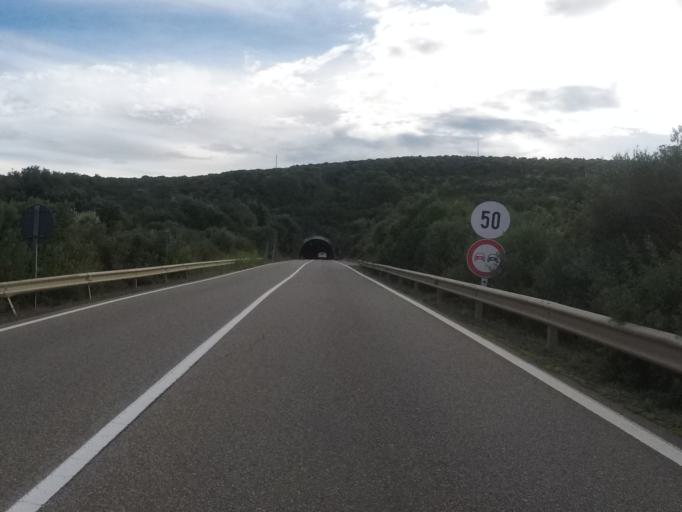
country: IT
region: Sardinia
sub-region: Provincia di Carbonia-Iglesias
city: Iglesias
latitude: 39.2949
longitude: 8.5429
